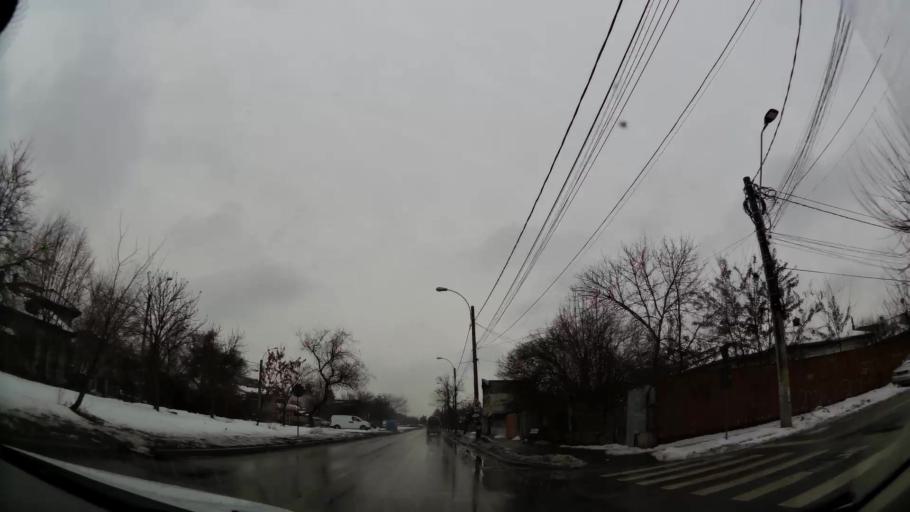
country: RO
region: Ilfov
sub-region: Comuna Chiajna
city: Rosu
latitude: 44.4917
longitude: 26.0279
